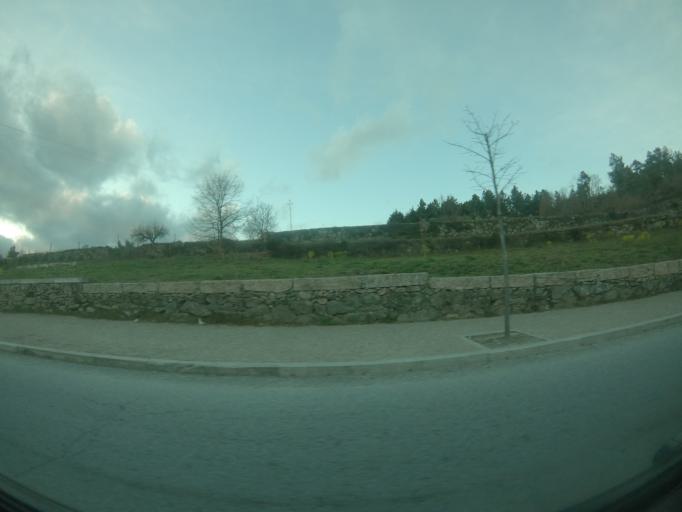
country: PT
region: Braganca
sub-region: Carrazeda de Ansiaes
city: Carrazeda de Anciaes
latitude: 41.2463
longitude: -7.3012
